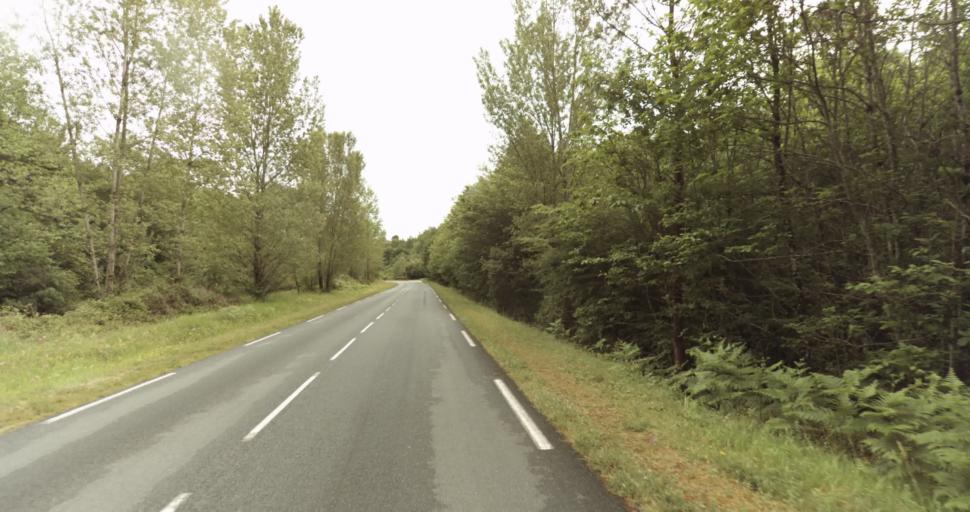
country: FR
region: Aquitaine
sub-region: Departement de la Dordogne
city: Belves
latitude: 44.6673
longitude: 1.0052
